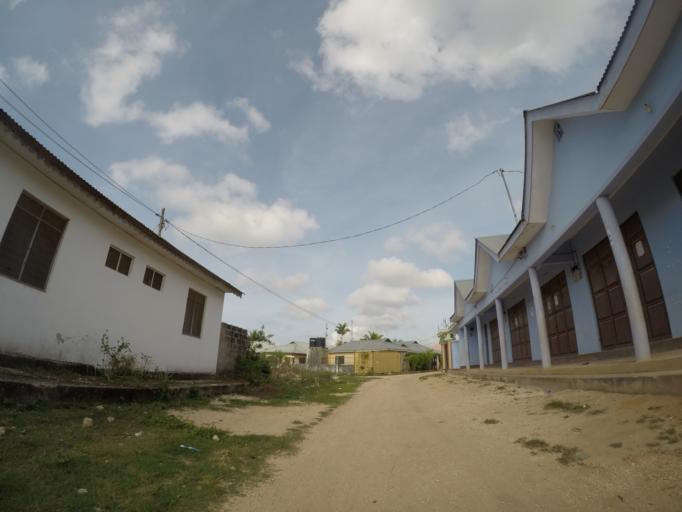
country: TZ
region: Zanzibar Central/South
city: Koani
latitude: -6.2274
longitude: 39.3145
